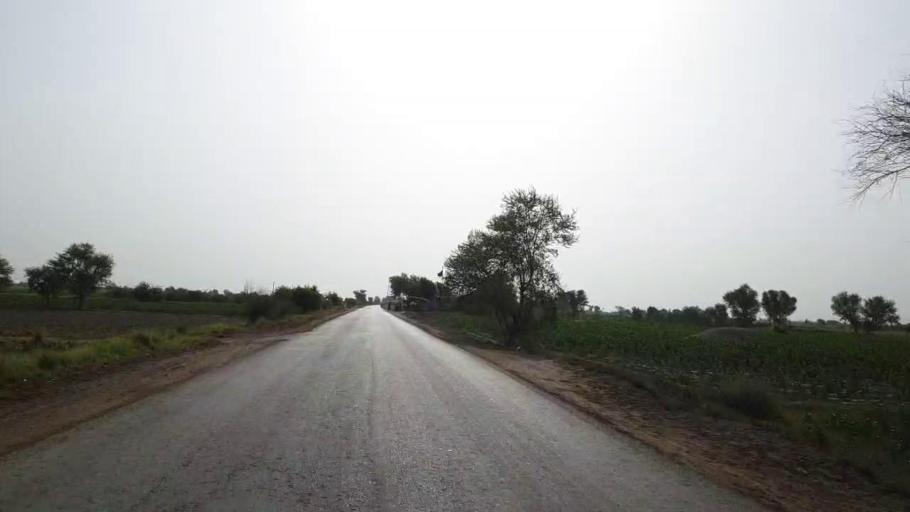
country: PK
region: Sindh
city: Nawabshah
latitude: 26.2664
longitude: 68.5116
